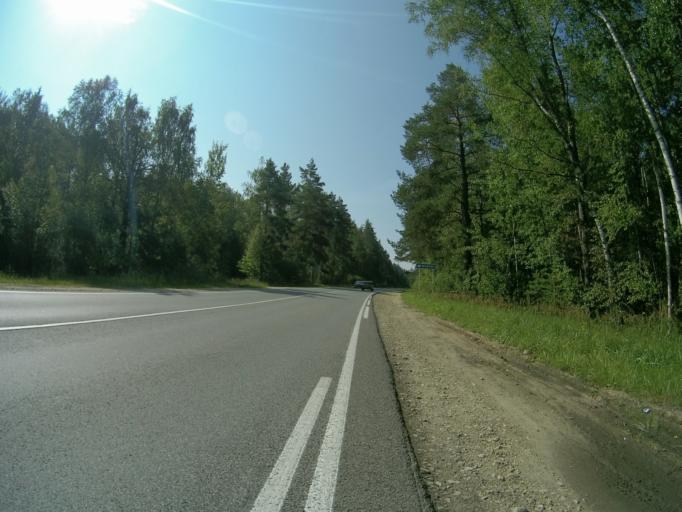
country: RU
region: Vladimir
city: Anopino
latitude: 55.8945
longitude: 40.6197
